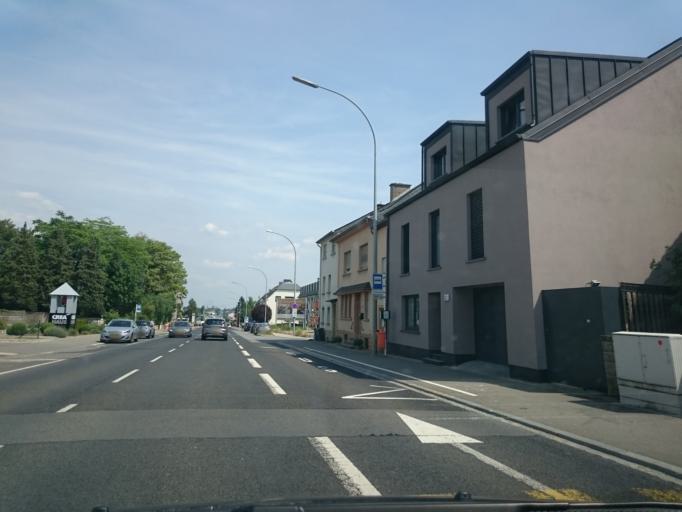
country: LU
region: Luxembourg
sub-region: Canton de Luxembourg
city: Strassen
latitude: 49.6217
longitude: 6.0614
